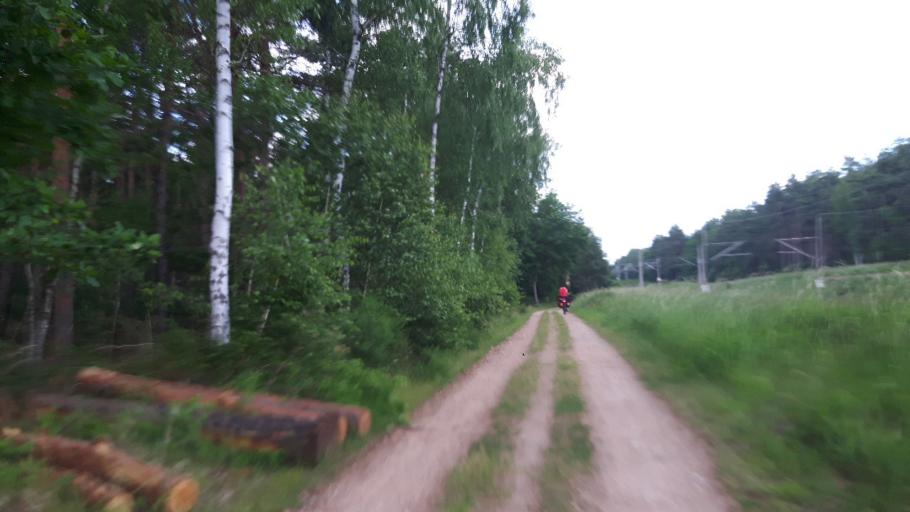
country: DE
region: Saxony-Anhalt
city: Radis
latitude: 51.7784
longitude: 12.5387
